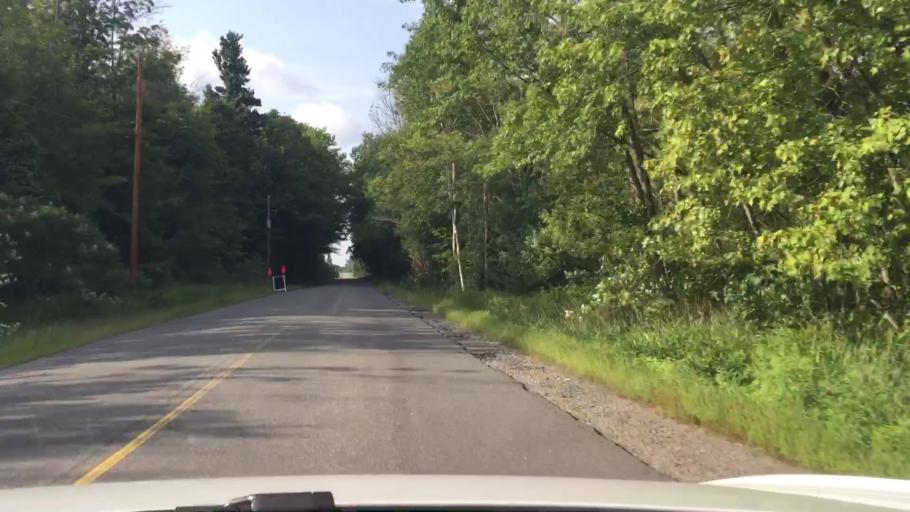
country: CA
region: Ontario
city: Oshawa
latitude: 43.9450
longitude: -78.7499
